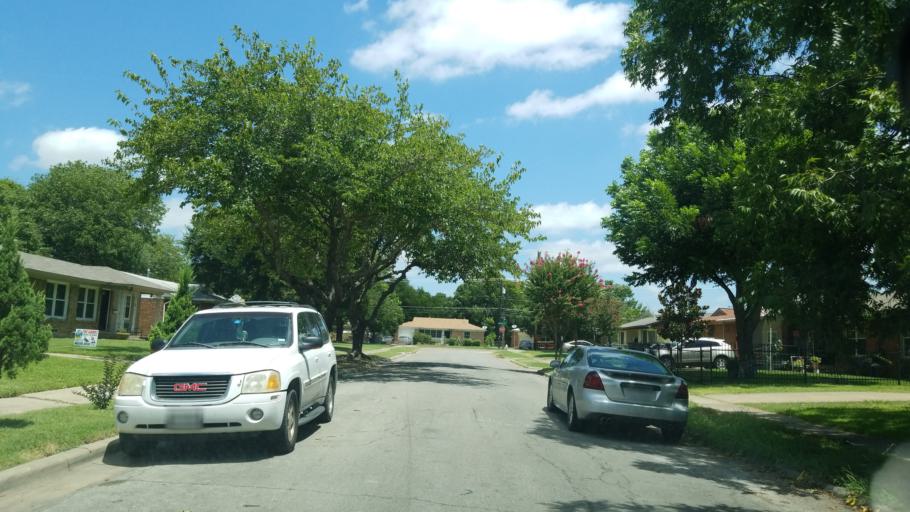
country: US
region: Texas
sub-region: Dallas County
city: Balch Springs
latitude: 32.7481
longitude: -96.6973
